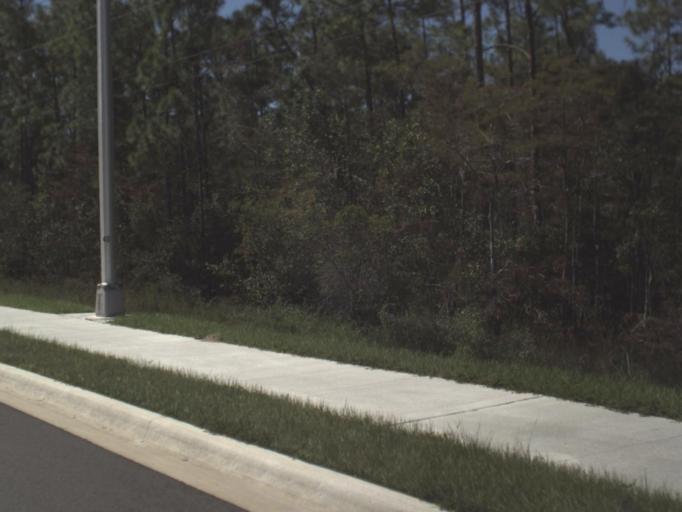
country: US
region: Florida
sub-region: Collier County
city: Golden Gate
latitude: 26.1459
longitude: -81.7035
